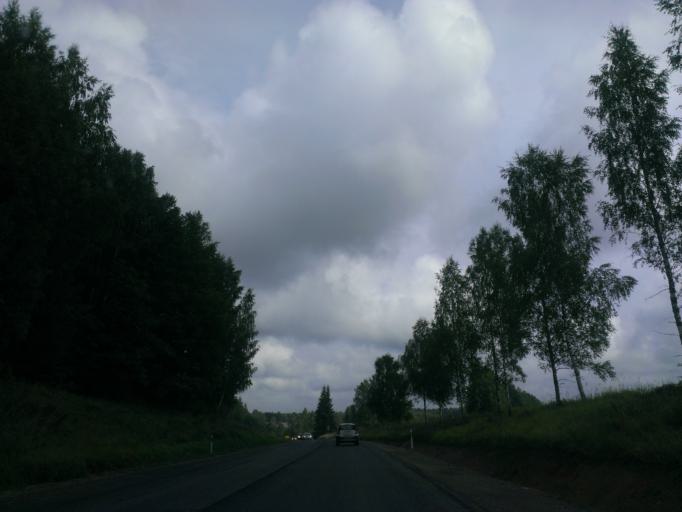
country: LV
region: Ligatne
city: Ligatne
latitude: 57.2040
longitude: 25.1432
